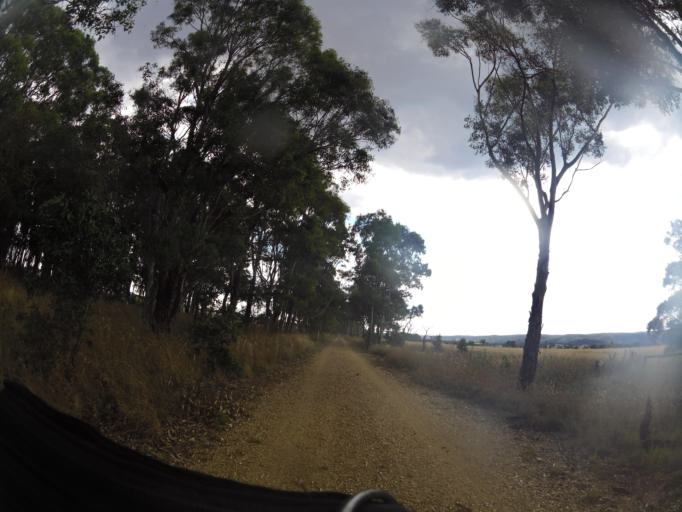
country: AU
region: Victoria
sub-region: Wellington
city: Heyfield
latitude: -38.0174
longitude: 146.6865
